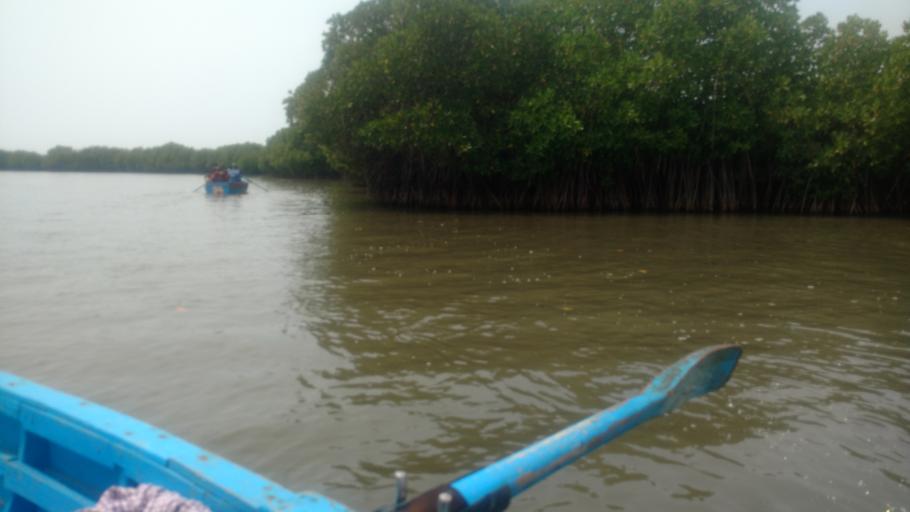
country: IN
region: Tamil Nadu
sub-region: Cuddalore
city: Annamalainagar
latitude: 11.4310
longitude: 79.7882
